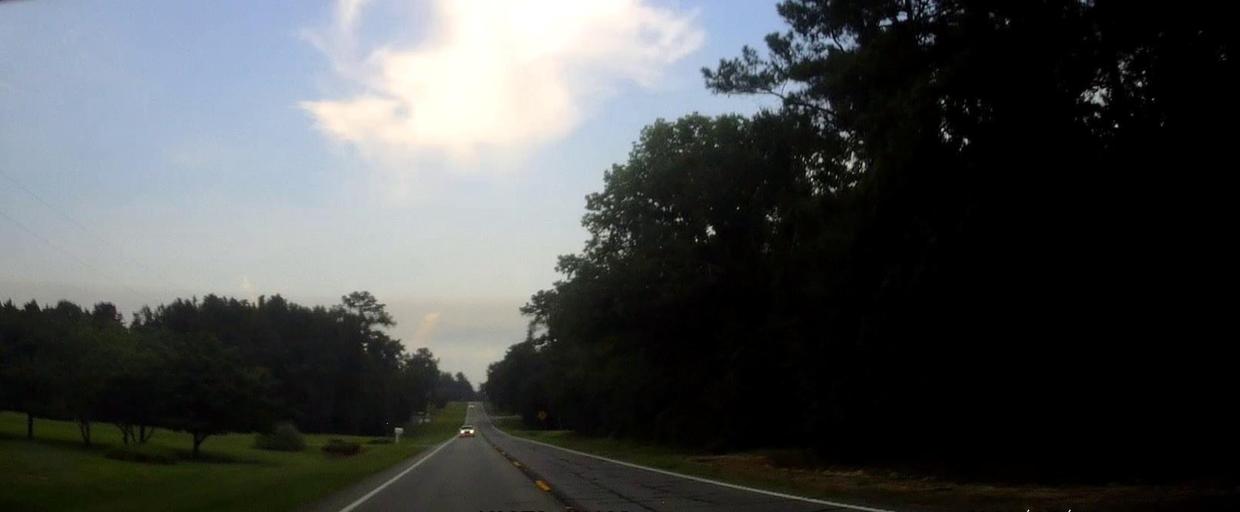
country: US
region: Georgia
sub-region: Laurens County
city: East Dublin
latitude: 32.6276
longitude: -82.8097
